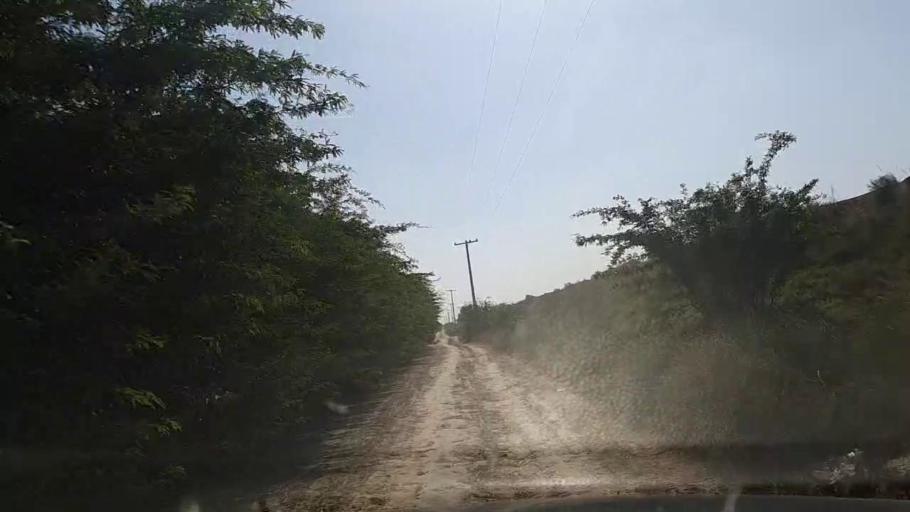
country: PK
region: Sindh
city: Daro Mehar
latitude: 24.7793
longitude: 68.0699
